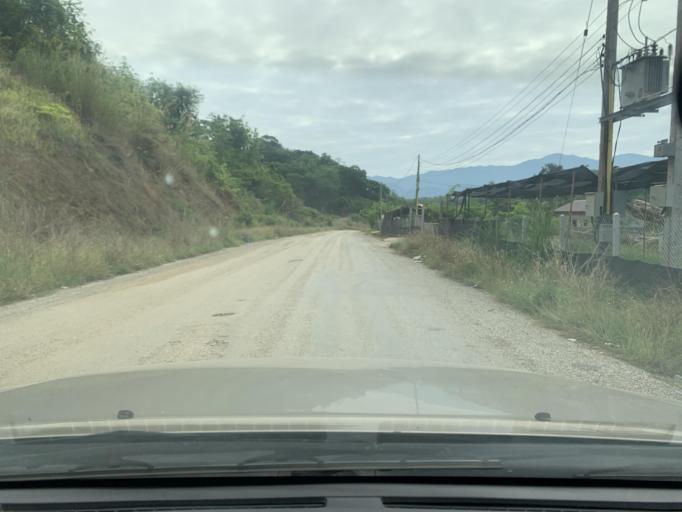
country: LA
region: Louangphabang
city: Louangphabang
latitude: 19.8863
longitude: 102.1801
